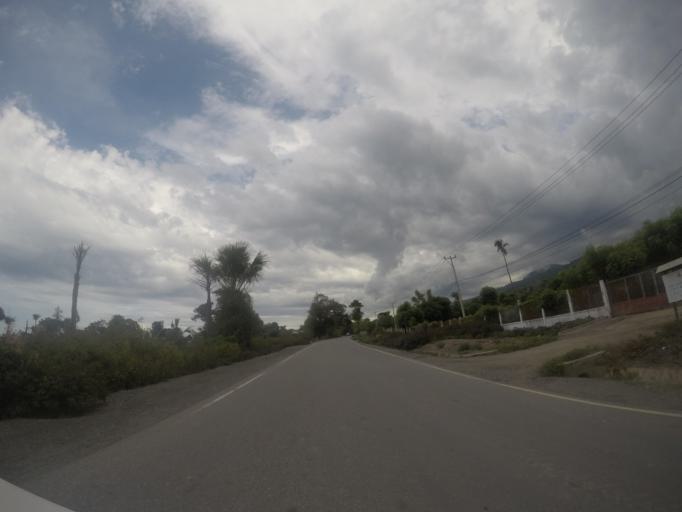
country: TL
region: Liquica
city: Liquica
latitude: -8.6037
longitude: 125.2969
